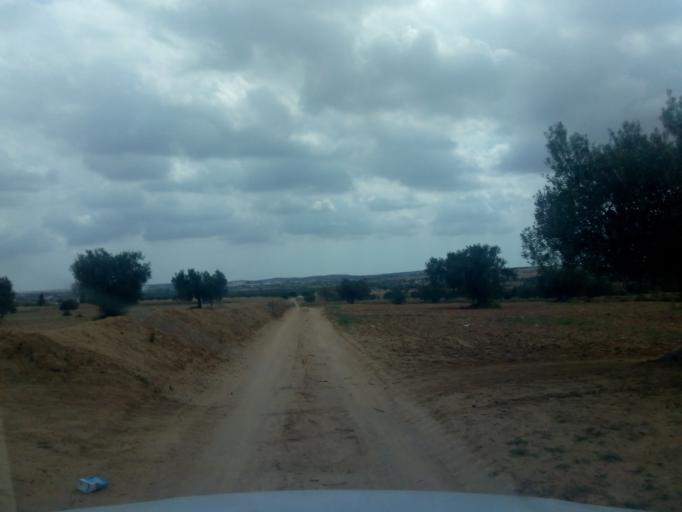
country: TN
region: Safaqis
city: Sfax
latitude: 34.7459
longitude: 10.4896
